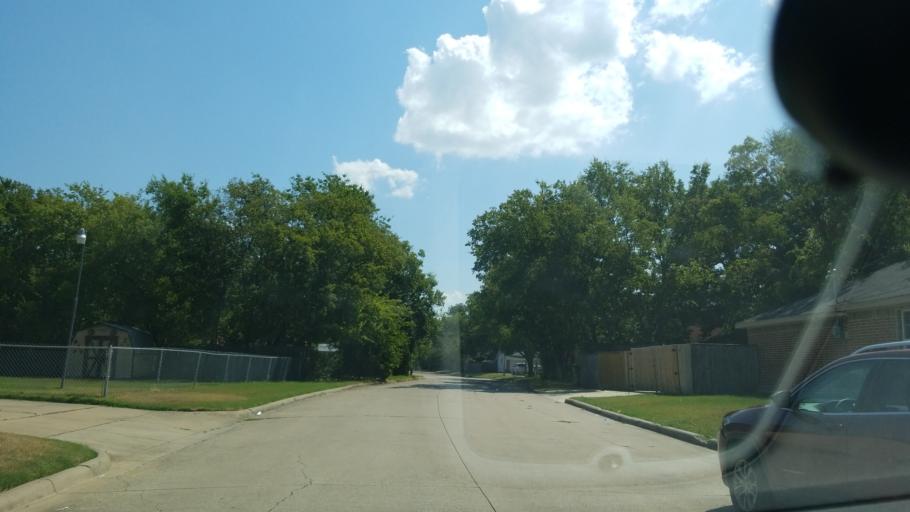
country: US
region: Texas
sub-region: Dallas County
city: Grand Prairie
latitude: 32.7138
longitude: -96.9843
